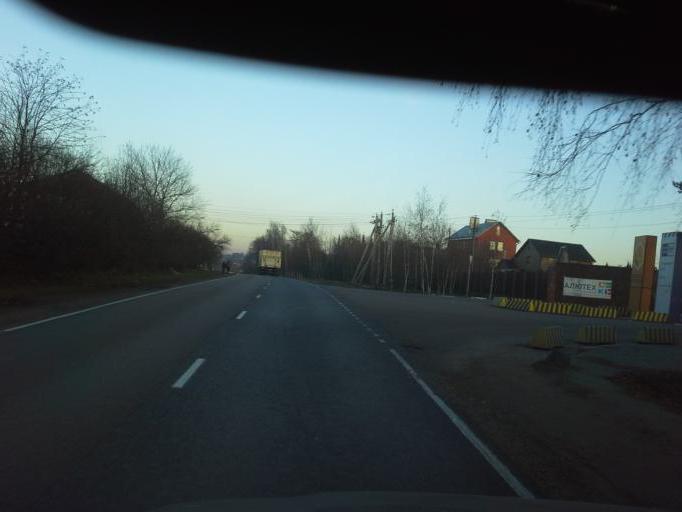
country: RU
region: Moskovskaya
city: Kokoshkino
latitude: 55.5843
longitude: 37.1823
